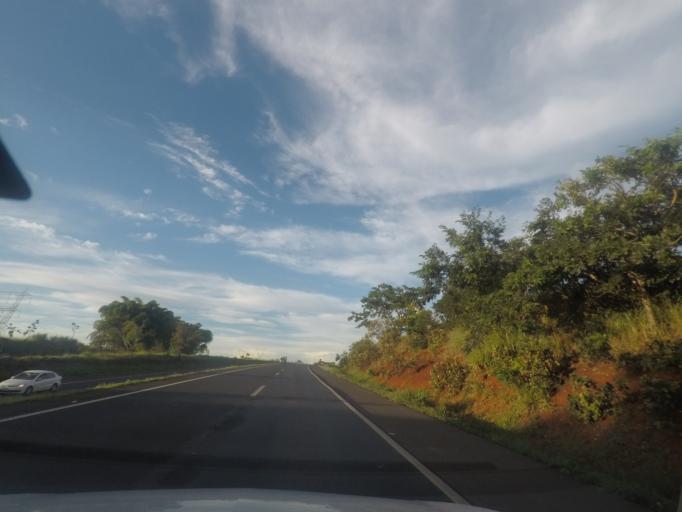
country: BR
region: Goias
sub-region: Goiatuba
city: Goiatuba
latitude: -18.0028
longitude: -49.2623
